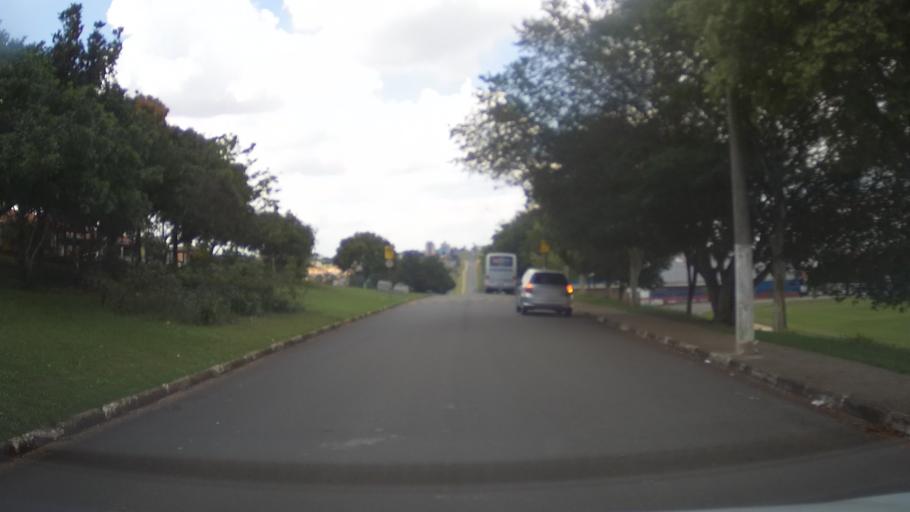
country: BR
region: Sao Paulo
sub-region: Valinhos
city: Valinhos
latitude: -22.9946
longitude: -46.9922
